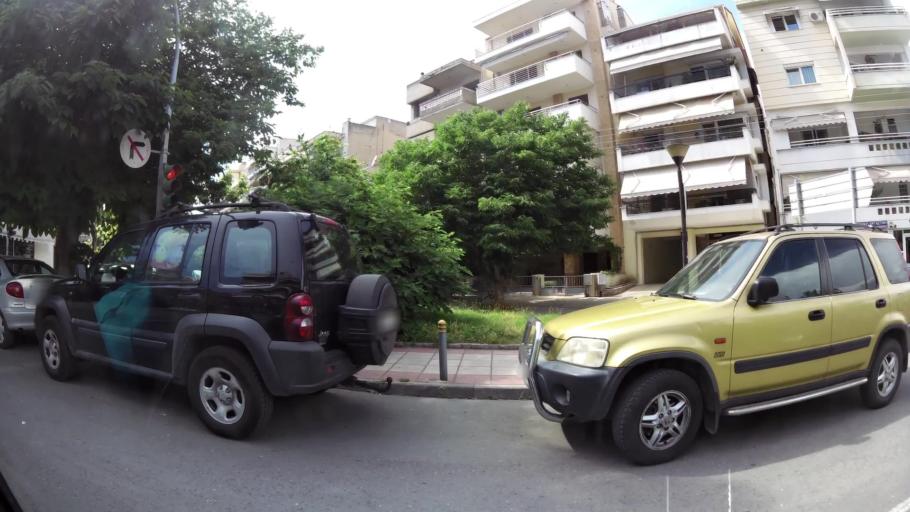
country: GR
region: Central Macedonia
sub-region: Nomos Thessalonikis
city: Kalamaria
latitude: 40.5872
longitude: 22.9492
